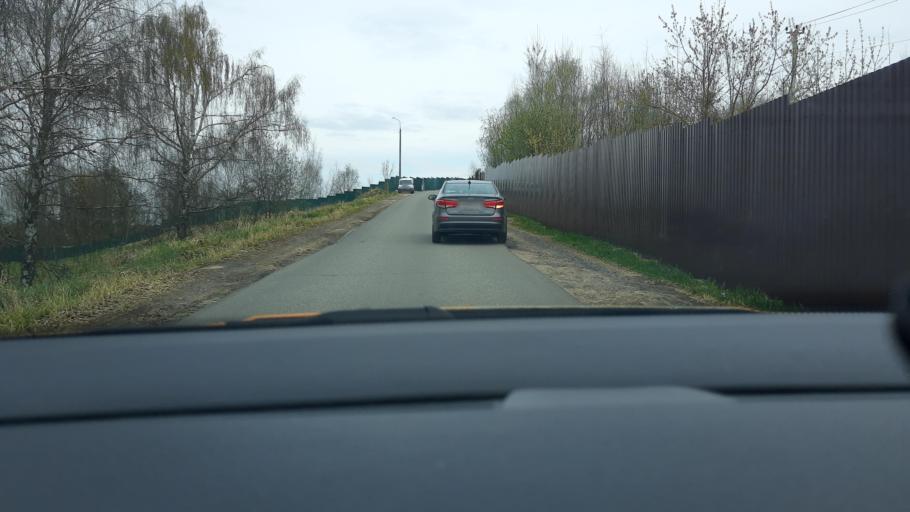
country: RU
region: Moskovskaya
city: Novopodrezkovo
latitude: 55.9252
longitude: 37.3498
